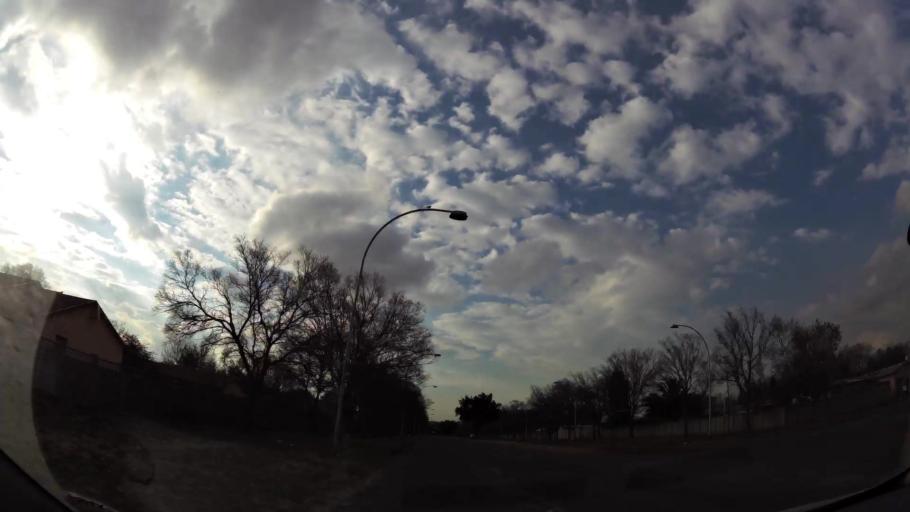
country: ZA
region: Orange Free State
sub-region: Fezile Dabi District Municipality
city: Sasolburg
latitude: -26.8144
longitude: 27.8091
